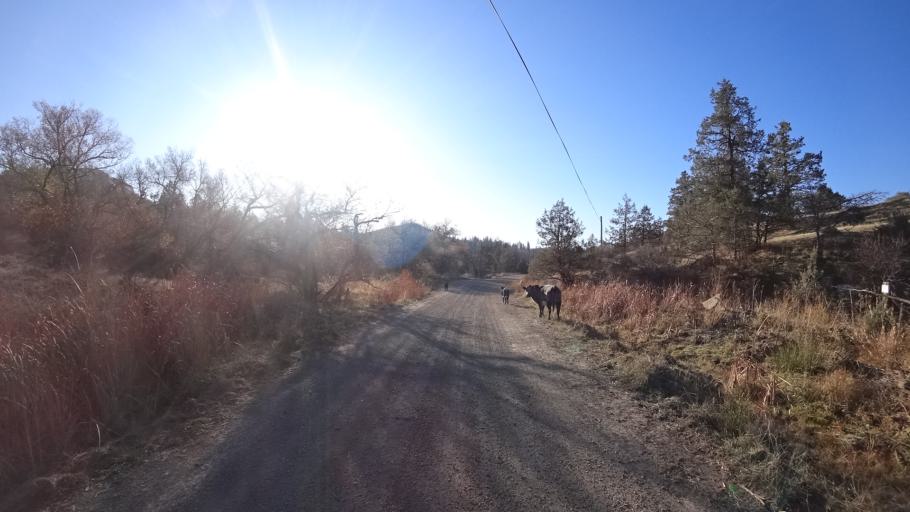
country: US
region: Oregon
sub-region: Jackson County
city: Ashland
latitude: 41.9898
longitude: -122.6230
